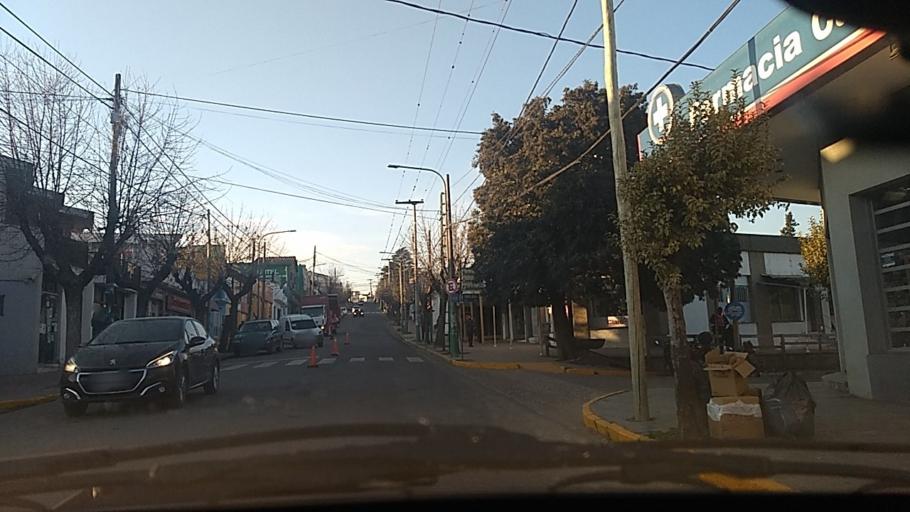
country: AR
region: Cordoba
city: Salsipuedes
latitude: -31.1376
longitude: -64.2930
